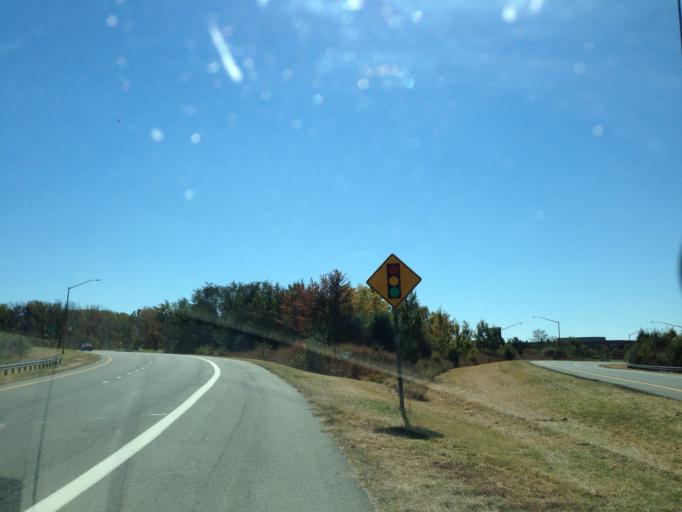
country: US
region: Maryland
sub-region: Montgomery County
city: Germantown
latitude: 39.1978
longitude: -77.2666
